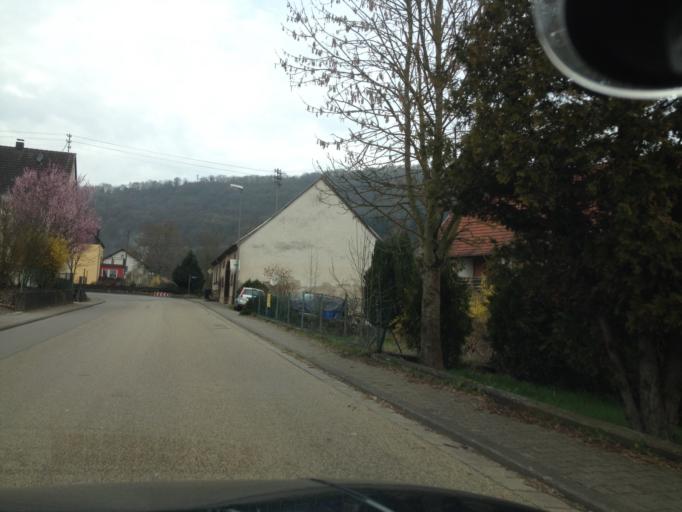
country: DE
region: Rheinland-Pfalz
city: Ruthweiler
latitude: 49.5524
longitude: 7.3674
